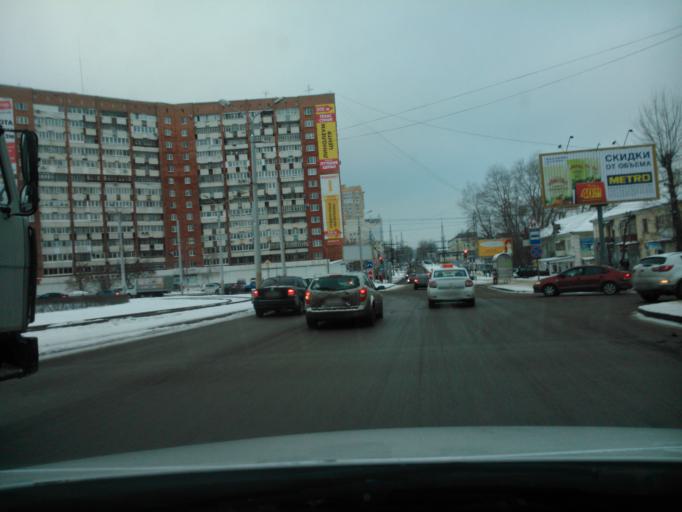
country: RU
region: Perm
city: Perm
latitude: 57.9868
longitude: 56.2142
